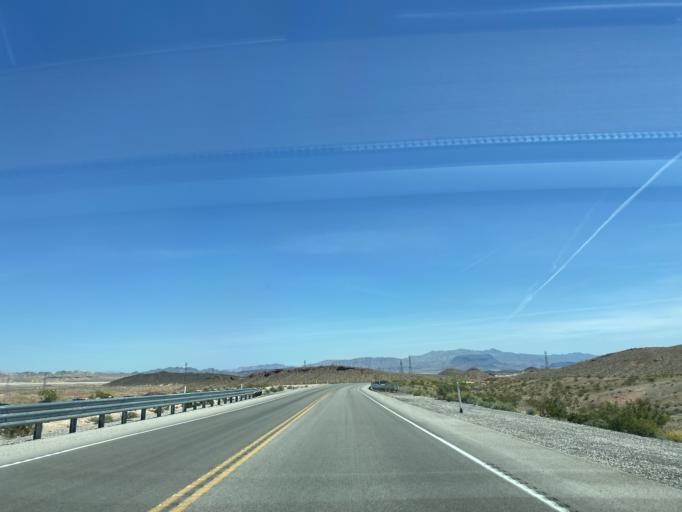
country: US
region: Nevada
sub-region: Clark County
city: Nellis Air Force Base
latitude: 36.1958
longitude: -114.9273
